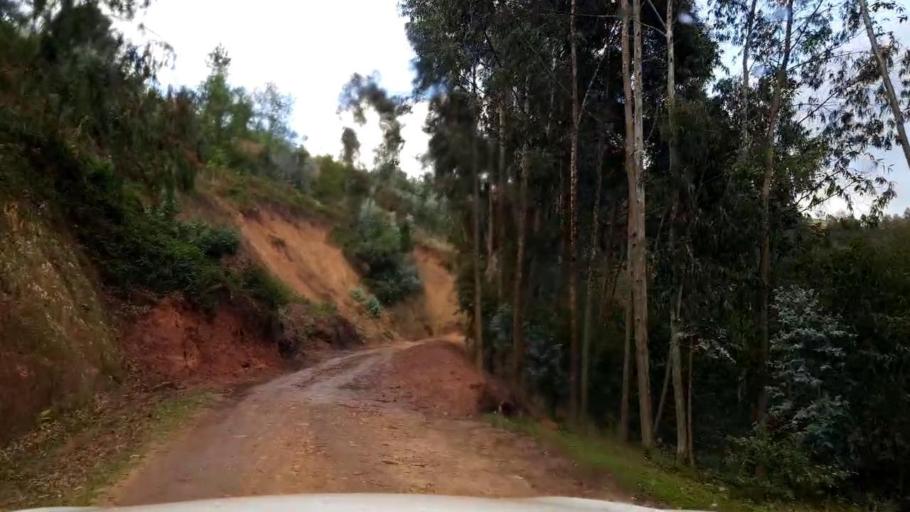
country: RW
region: Southern Province
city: Gitarama
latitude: -1.8652
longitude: 29.5698
